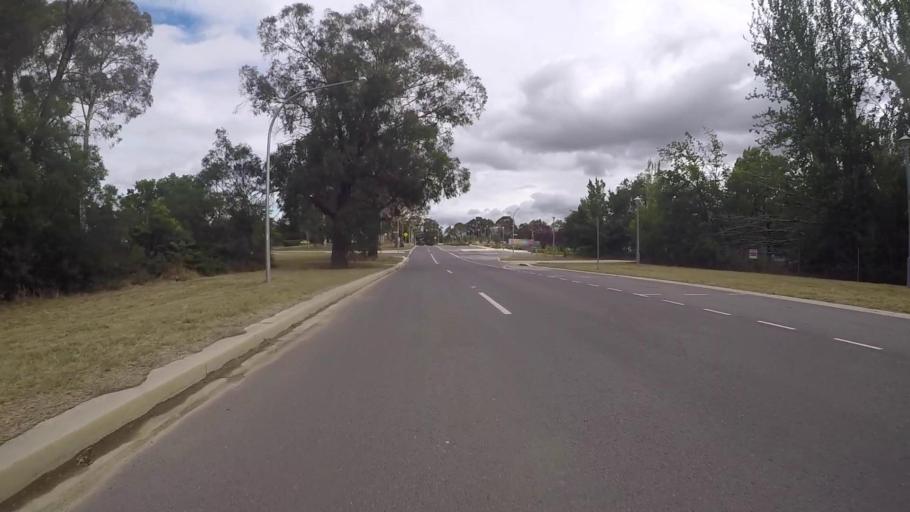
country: AU
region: Australian Capital Territory
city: Forrest
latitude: -35.3155
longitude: 149.1504
